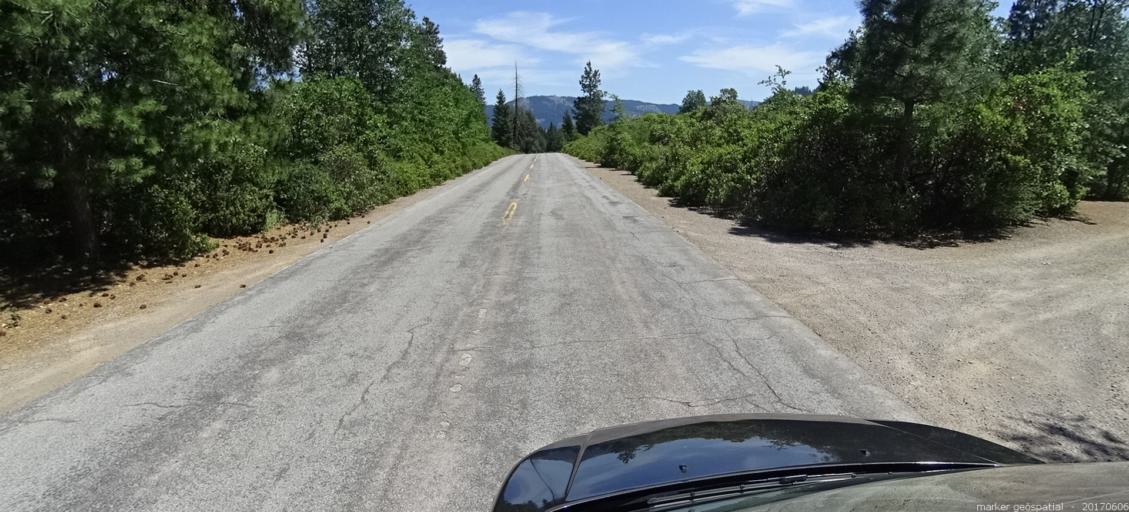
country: US
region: California
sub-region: Siskiyou County
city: Mount Shasta
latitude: 41.2821
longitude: -122.2933
